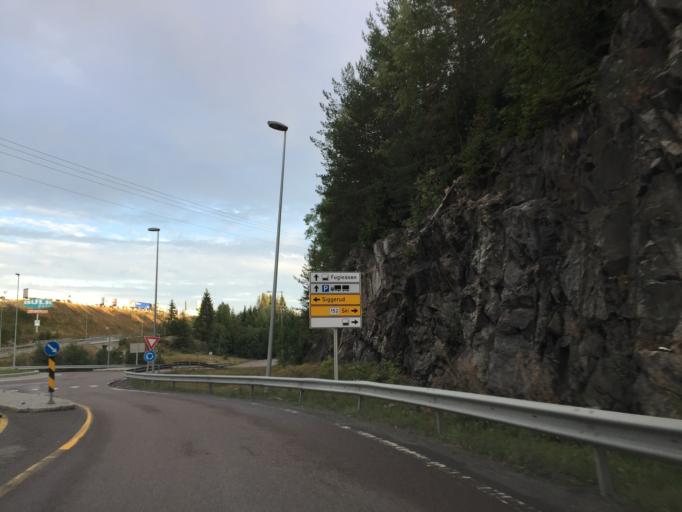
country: NO
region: Akershus
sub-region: Oppegard
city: Kolbotn
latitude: 59.7758
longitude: 10.8501
